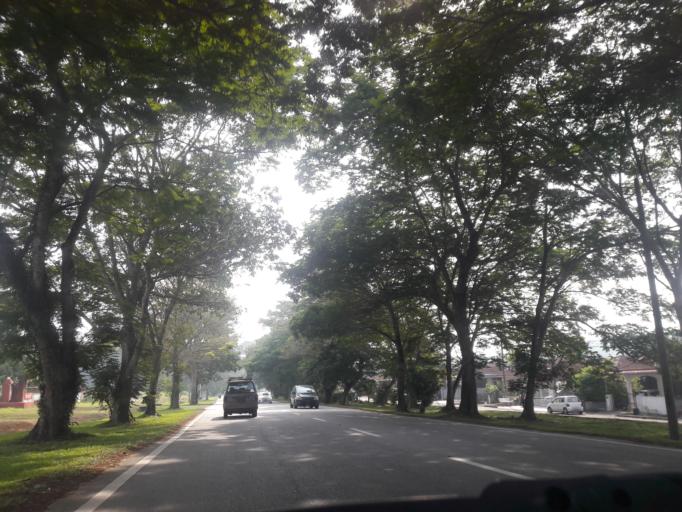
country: MY
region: Kedah
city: Kulim
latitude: 5.3487
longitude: 100.5240
